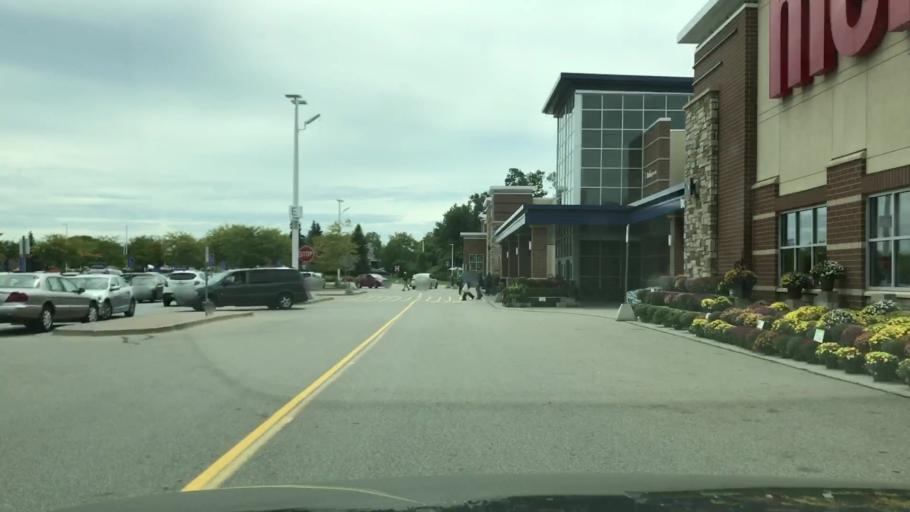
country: US
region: Michigan
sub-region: Kent County
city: Northview
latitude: 42.9969
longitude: -85.5936
